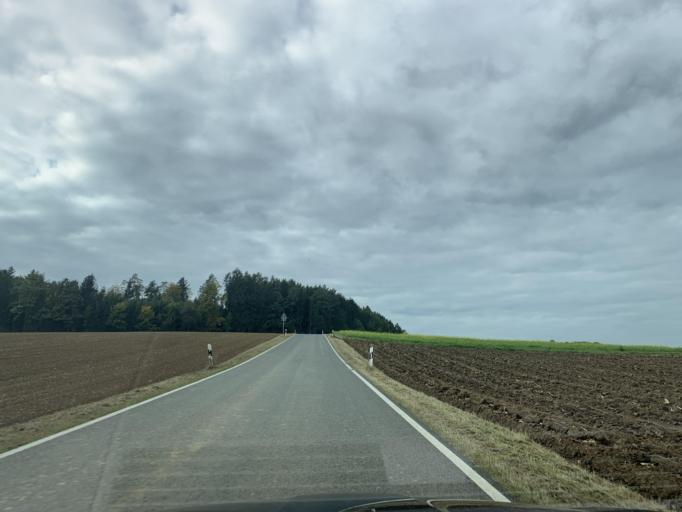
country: DE
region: Bavaria
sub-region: Upper Franconia
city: Aufsess
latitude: 49.8520
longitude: 11.2303
